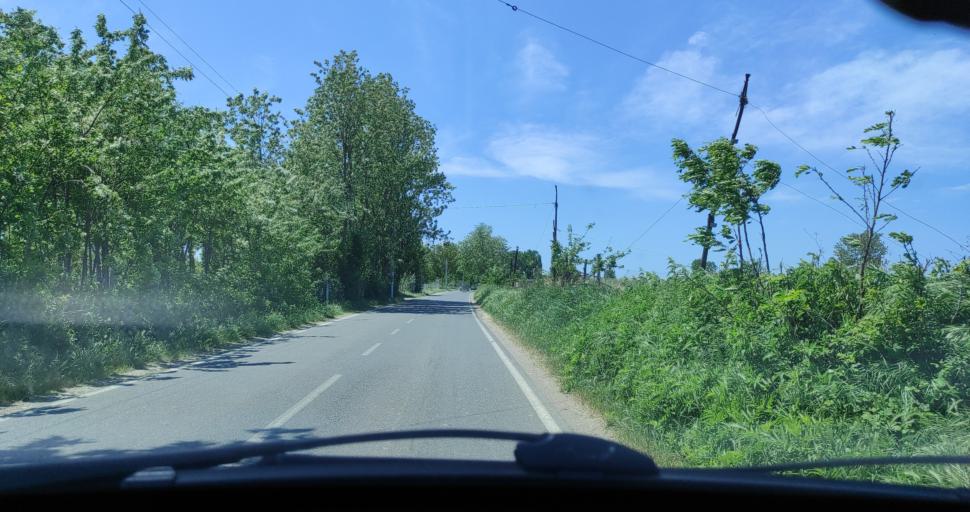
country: AL
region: Lezhe
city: Lezhe
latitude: 41.7627
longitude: 19.6320
